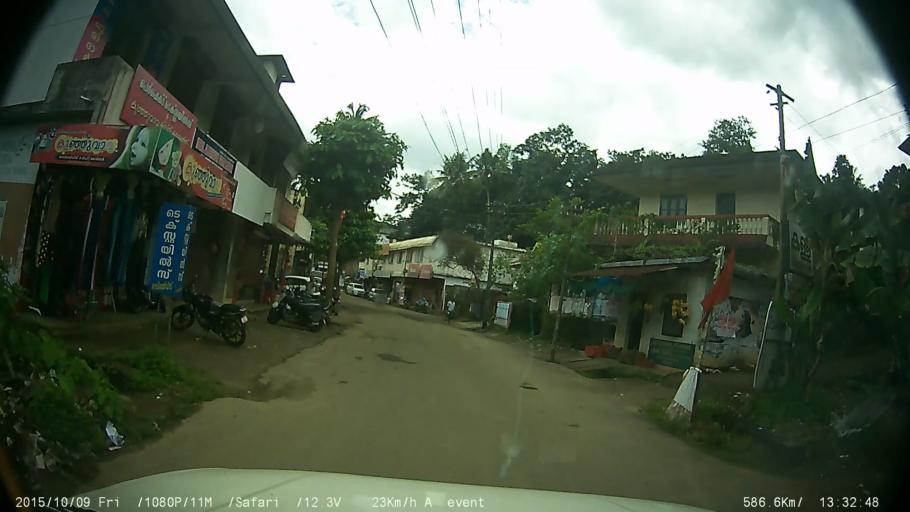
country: IN
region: Kerala
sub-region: Ernakulam
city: Ramamangalam
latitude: 9.9095
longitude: 76.5582
